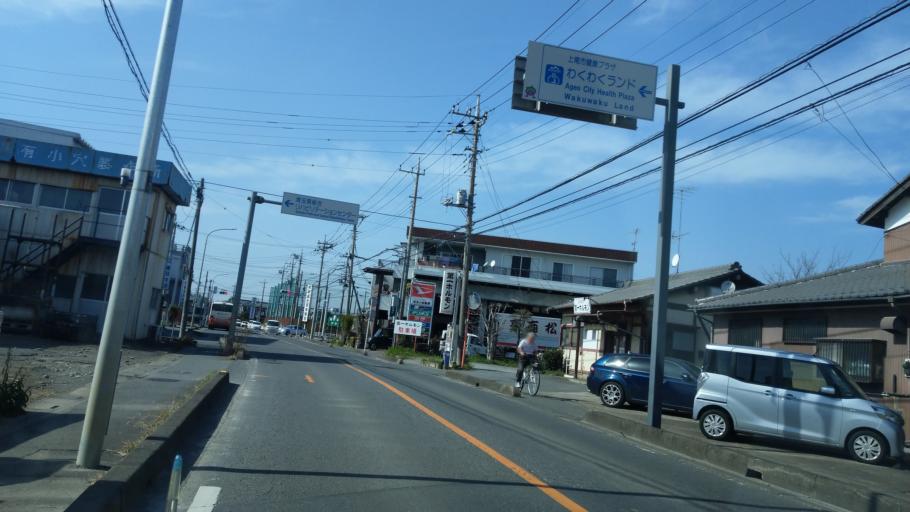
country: JP
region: Saitama
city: Okegawa
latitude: 35.9382
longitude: 139.5558
